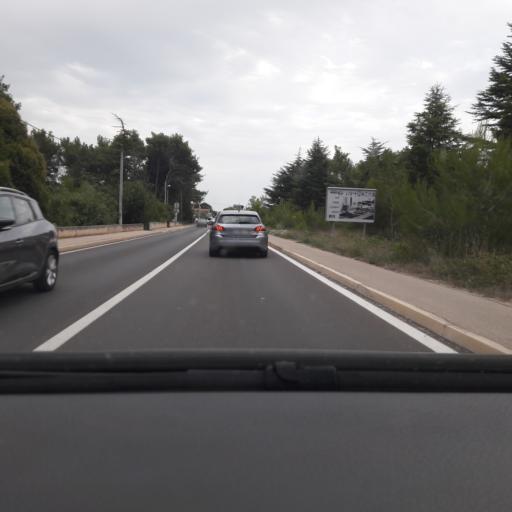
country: HR
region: Zadarska
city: Nin
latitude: 44.1748
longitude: 15.1911
